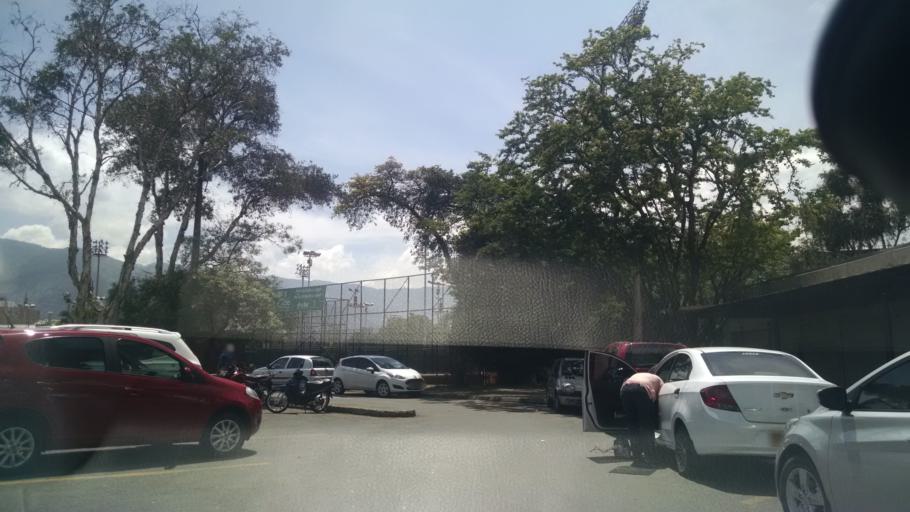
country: CO
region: Antioquia
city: Medellin
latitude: 6.2584
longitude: -75.5906
